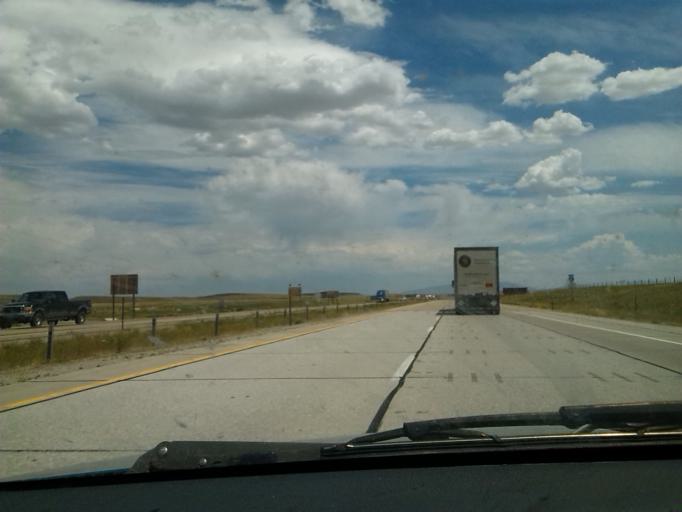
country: US
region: Wyoming
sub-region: Carbon County
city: Rawlins
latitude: 41.7877
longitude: -107.1887
